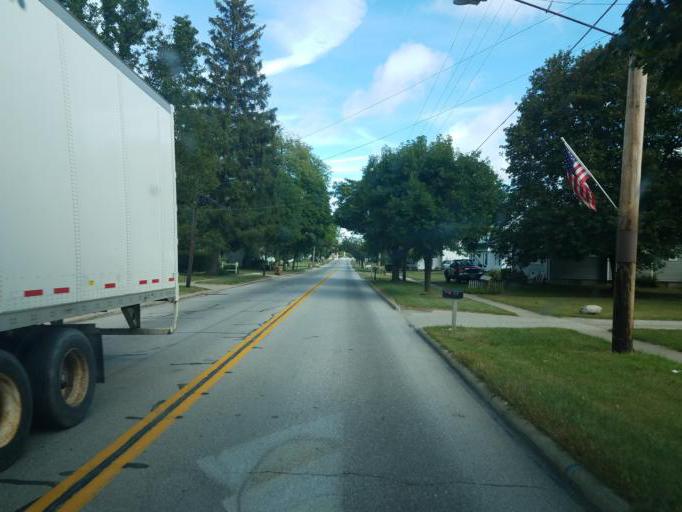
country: US
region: Ohio
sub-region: Lorain County
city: Wellington
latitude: 41.0969
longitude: -82.1233
